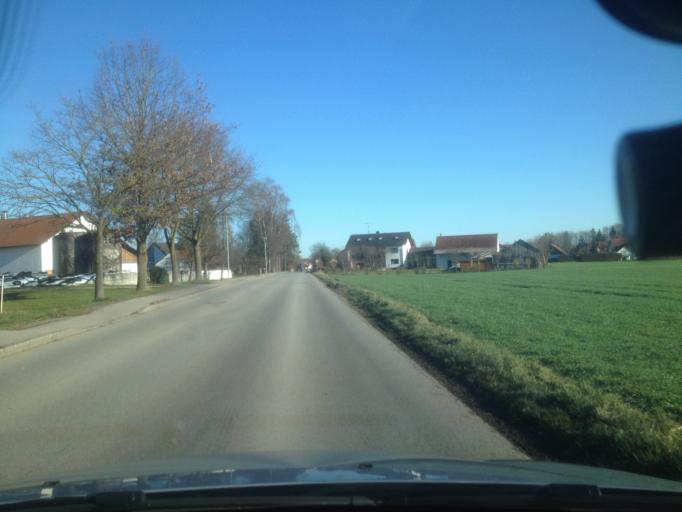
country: DE
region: Bavaria
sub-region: Upper Bavaria
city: Langenbach
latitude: 48.4100
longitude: 11.8739
